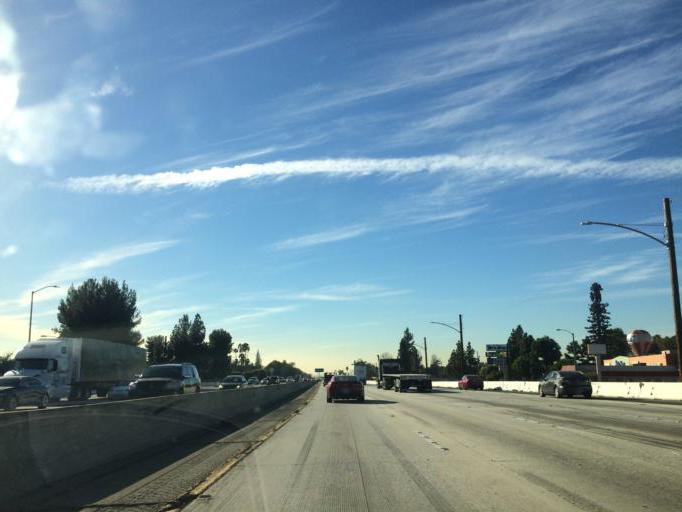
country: US
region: California
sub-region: Los Angeles County
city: West Covina
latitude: 34.0724
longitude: -117.9407
